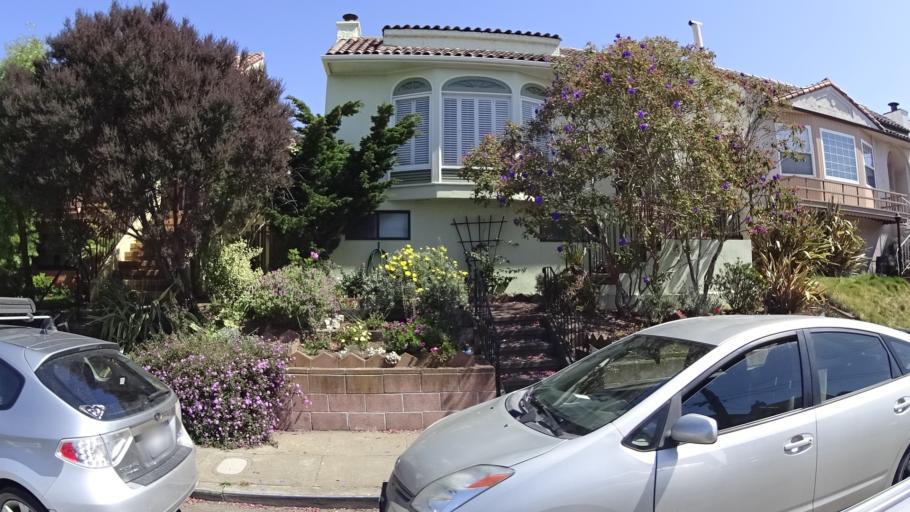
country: US
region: California
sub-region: San Mateo County
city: Daly City
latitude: 37.7536
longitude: -122.4743
